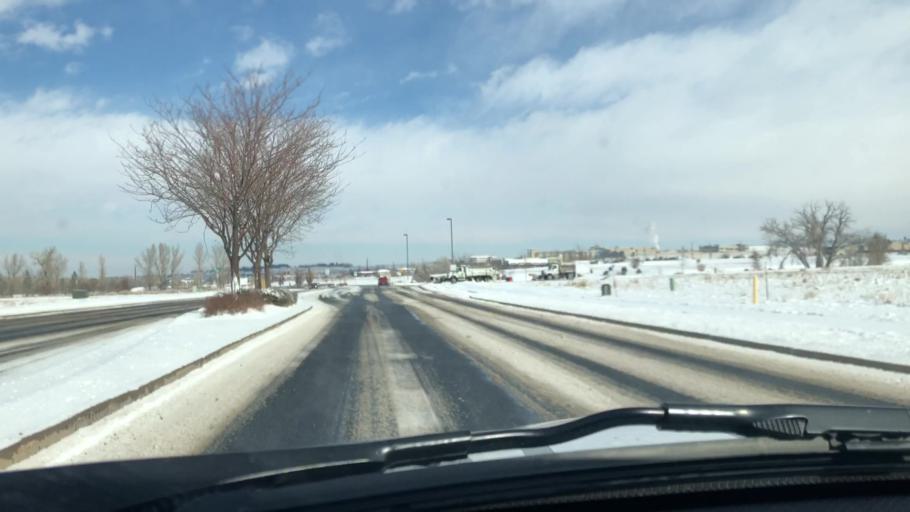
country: US
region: Colorado
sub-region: Douglas County
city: Parker
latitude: 39.5390
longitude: -104.7745
